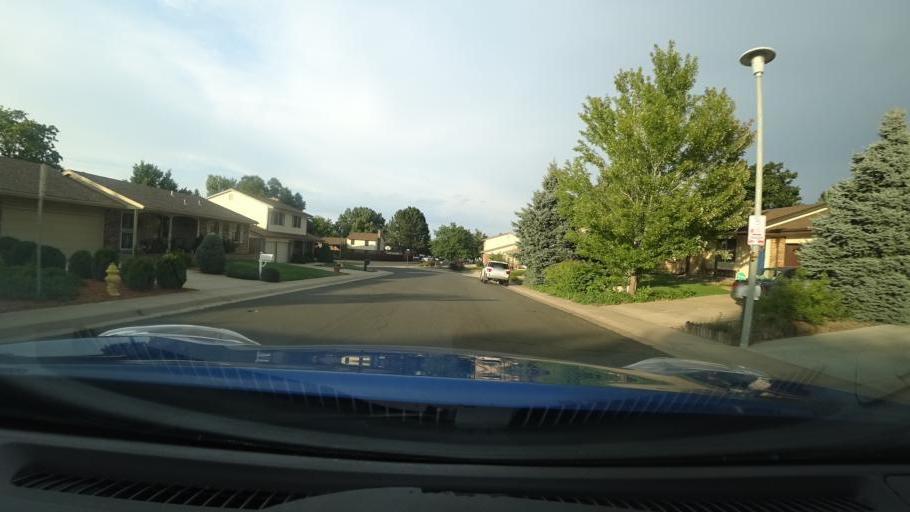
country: US
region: Colorado
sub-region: Adams County
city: Aurora
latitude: 39.6903
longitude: -104.8219
